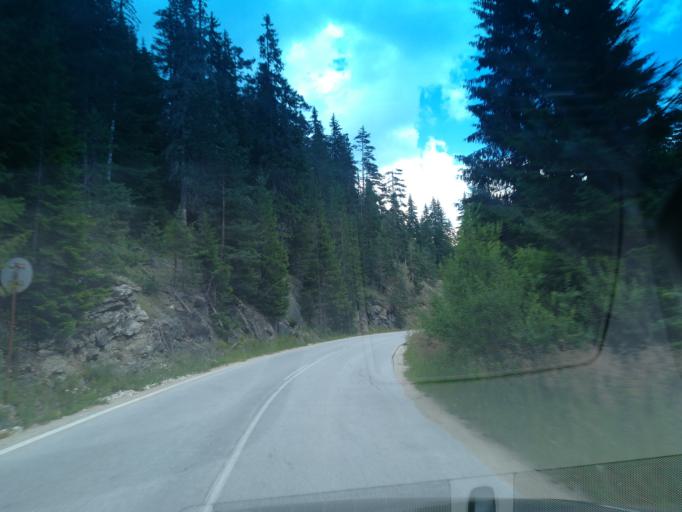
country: BG
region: Smolyan
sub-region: Obshtina Chepelare
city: Chepelare
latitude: 41.6617
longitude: 24.6682
